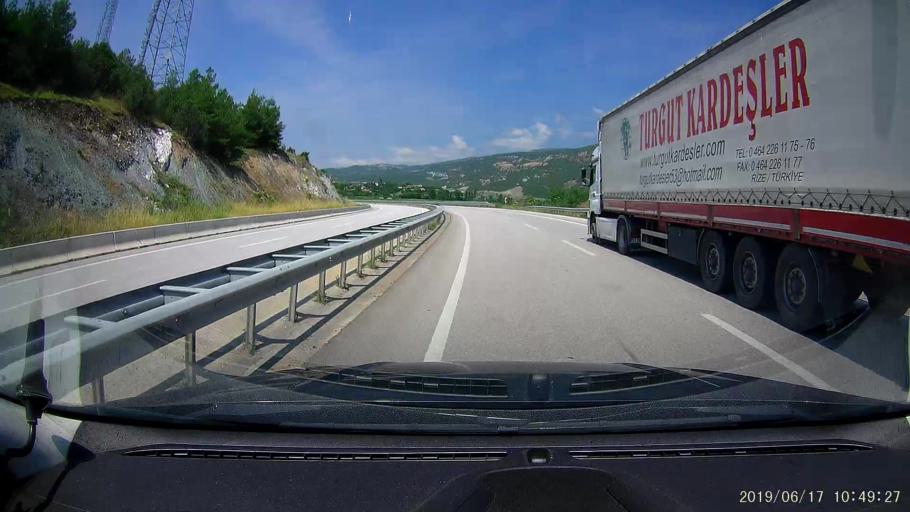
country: TR
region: Corum
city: Hacihamza
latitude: 41.1019
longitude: 34.4097
